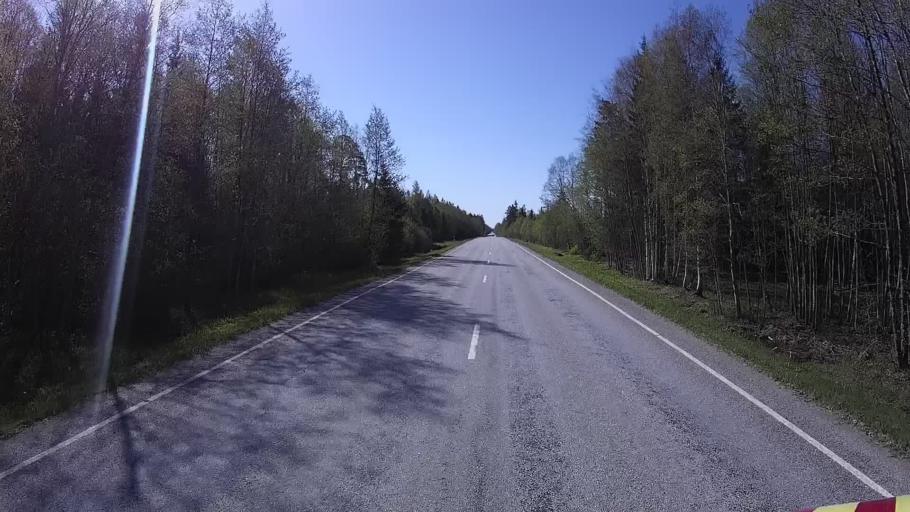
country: EE
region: Raplamaa
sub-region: Jaervakandi vald
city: Jarvakandi
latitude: 58.8151
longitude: 24.8044
